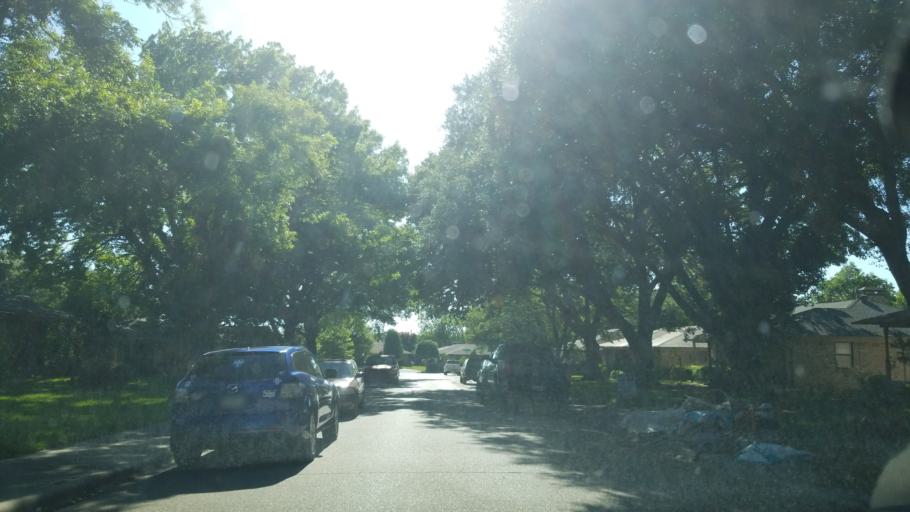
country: US
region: Texas
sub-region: Dallas County
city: Highland Park
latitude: 32.7916
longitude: -96.7087
